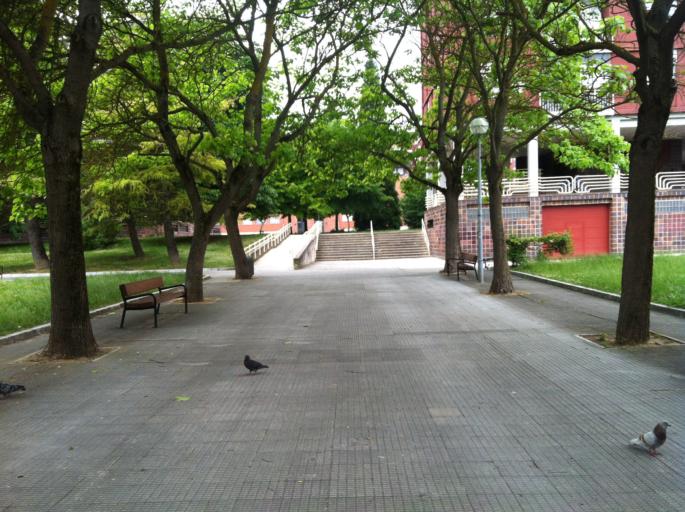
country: ES
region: Basque Country
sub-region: Provincia de Alava
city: Gasteiz / Vitoria
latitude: 42.8536
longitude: -2.6841
